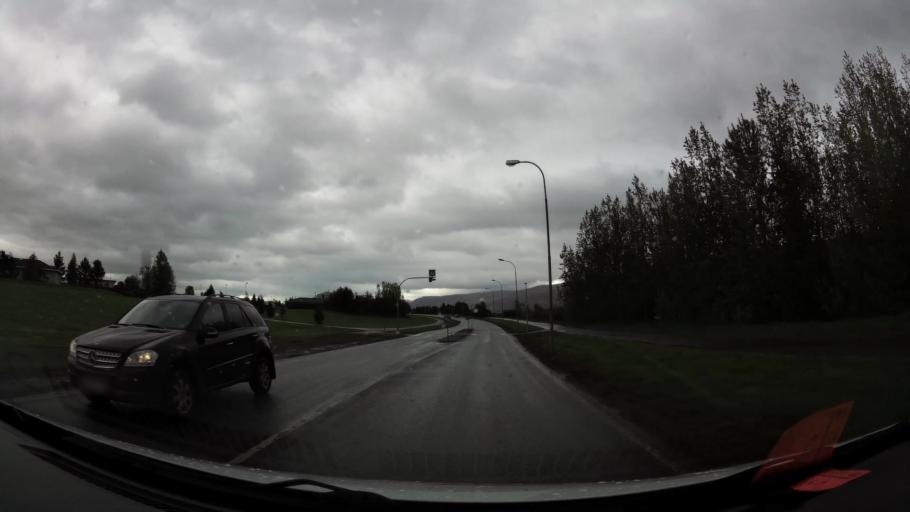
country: IS
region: Northeast
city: Akureyri
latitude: 65.6809
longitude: -18.1314
